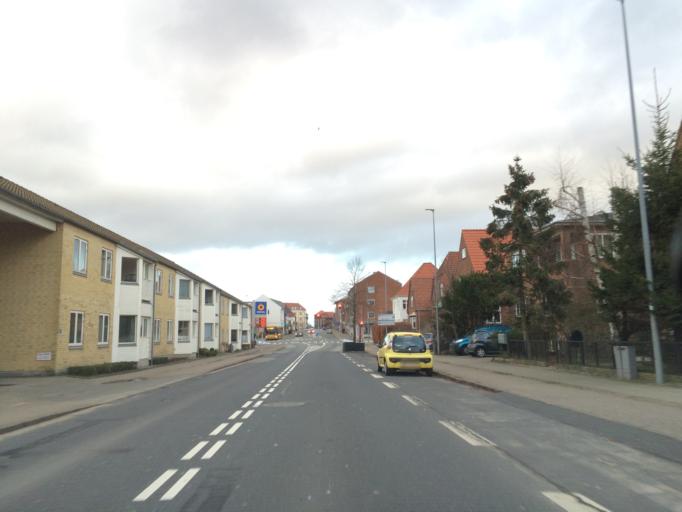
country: DK
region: Central Jutland
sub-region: Silkeborg Kommune
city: Silkeborg
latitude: 56.1618
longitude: 9.5506
